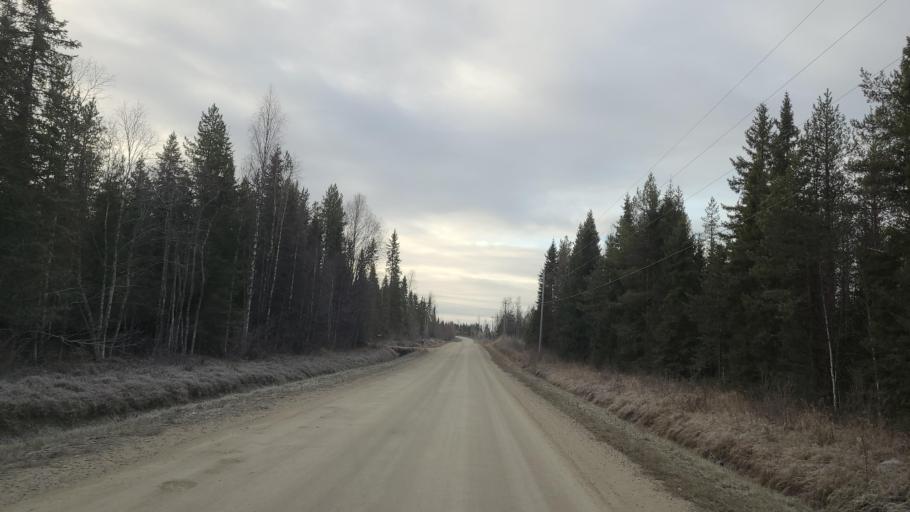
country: FI
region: Lapland
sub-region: Kemi-Tornio
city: Tervola
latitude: 66.0454
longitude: 25.0450
